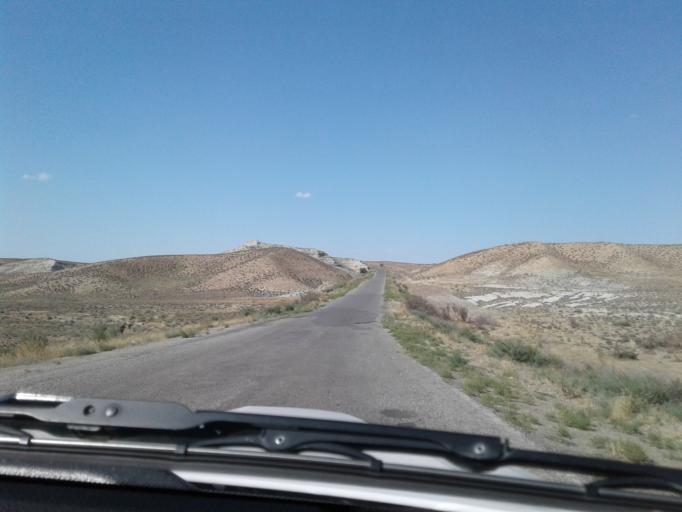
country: TM
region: Balkan
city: Magtymguly
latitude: 38.5270
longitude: 56.1905
